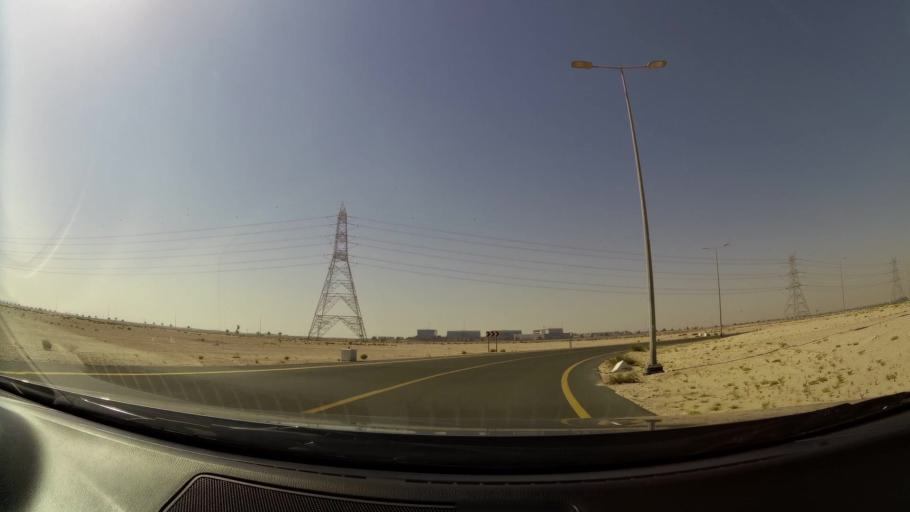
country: AE
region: Dubai
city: Dubai
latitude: 24.9020
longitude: 55.0665
